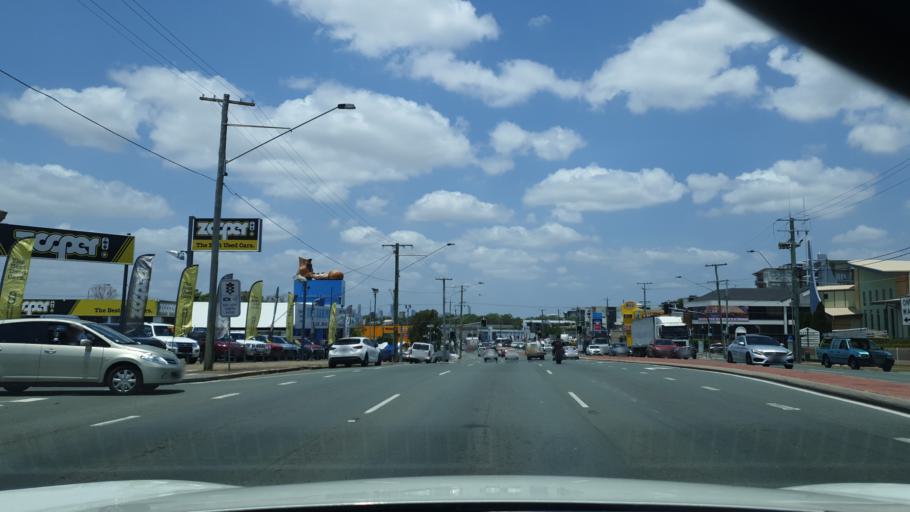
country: AU
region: Queensland
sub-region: Brisbane
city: Wavell Heights
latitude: -27.3924
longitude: 153.0312
